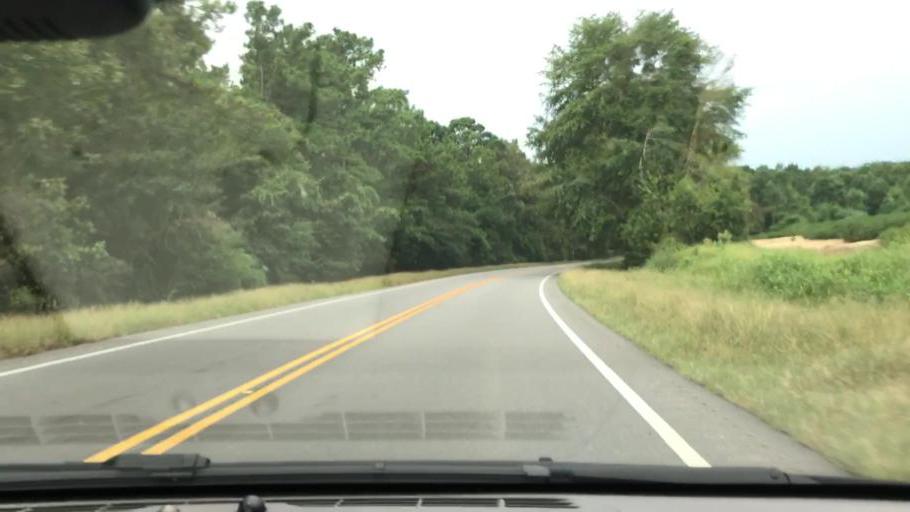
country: US
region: Alabama
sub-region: Houston County
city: Webb
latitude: 31.2759
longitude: -85.1495
